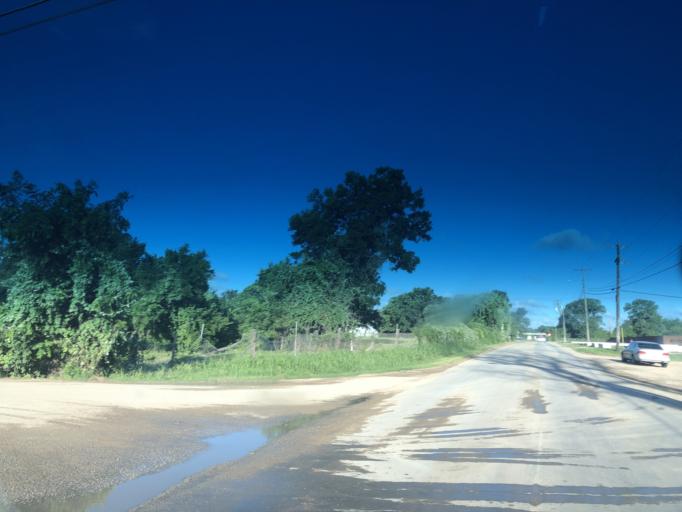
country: US
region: Texas
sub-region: Dallas County
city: Grand Prairie
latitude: 32.7924
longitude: -97.0090
